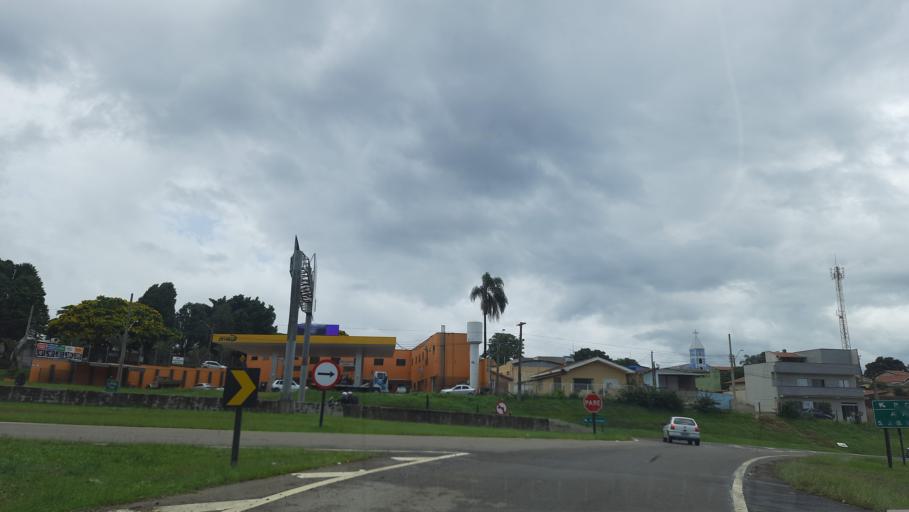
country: BR
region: Minas Gerais
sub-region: Pocos De Caldas
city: Pocos de Caldas
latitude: -21.8455
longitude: -46.6819
